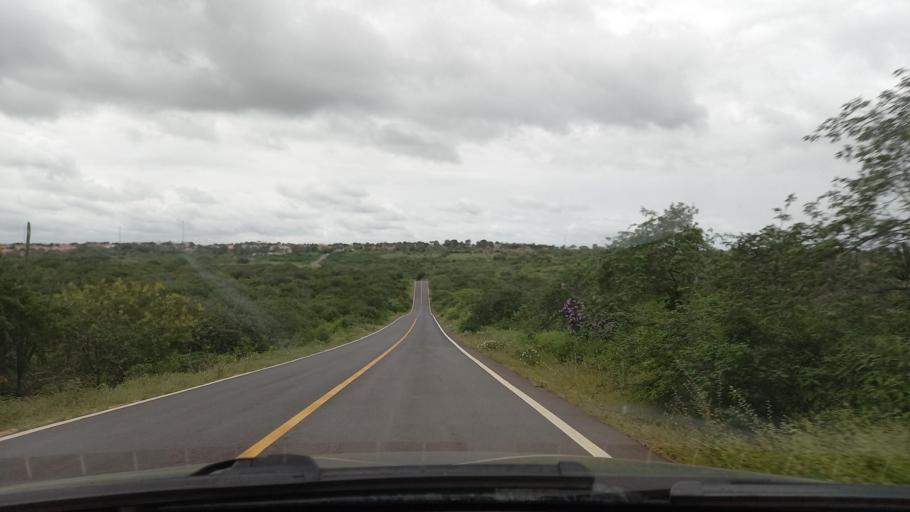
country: BR
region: Sergipe
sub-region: Caninde De Sao Francisco
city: Caninde de Sao Francisco
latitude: -9.6174
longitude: -37.7770
